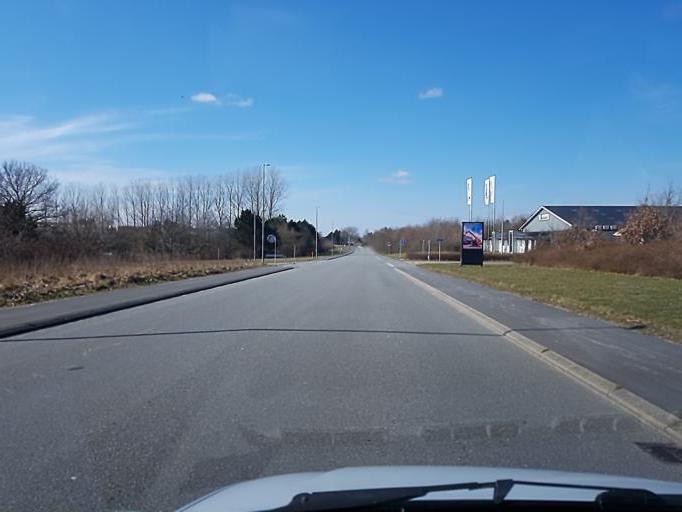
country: DK
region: South Denmark
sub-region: Varde Kommune
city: Varde
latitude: 55.6085
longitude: 8.5031
